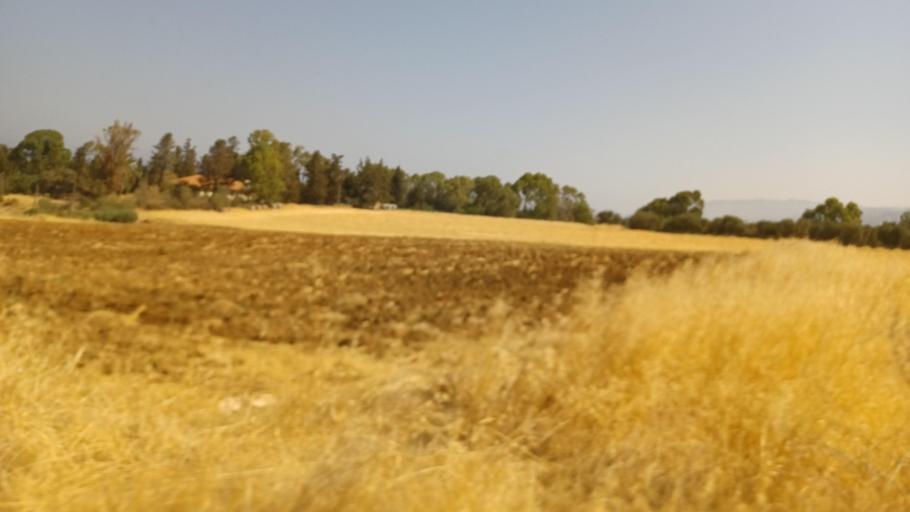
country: CY
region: Pafos
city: Polis
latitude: 35.0477
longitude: 32.4549
